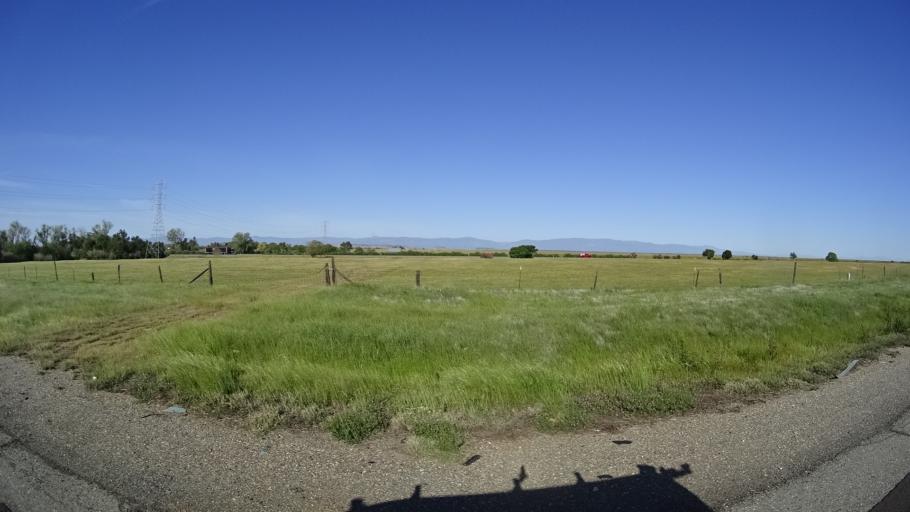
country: US
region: California
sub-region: Glenn County
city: Orland
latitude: 39.8021
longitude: -122.1974
